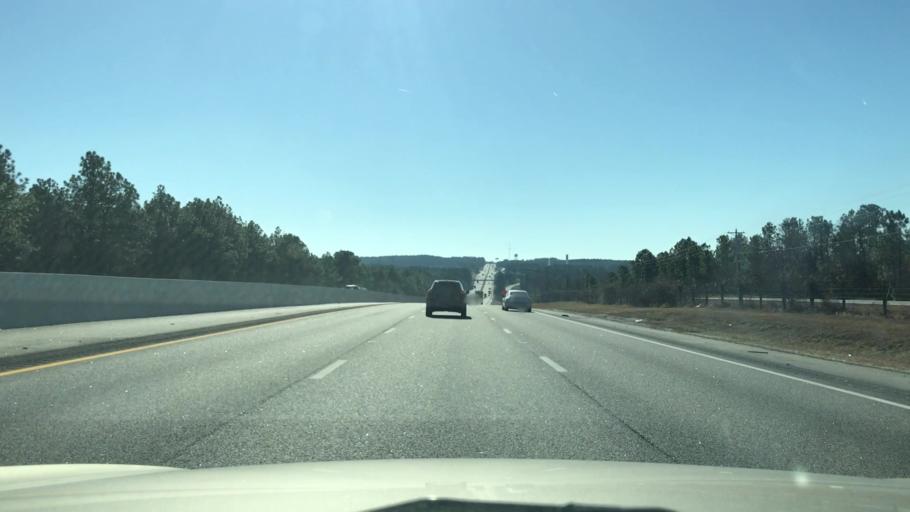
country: US
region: South Carolina
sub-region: Lexington County
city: Gaston
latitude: 33.8616
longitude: -81.0309
